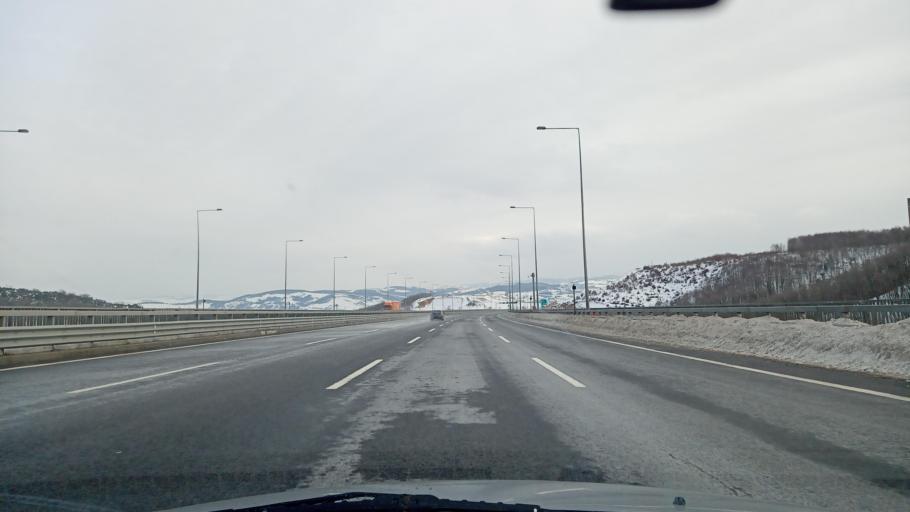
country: TR
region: Kocaeli
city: Korfez
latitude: 40.8892
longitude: 29.7302
